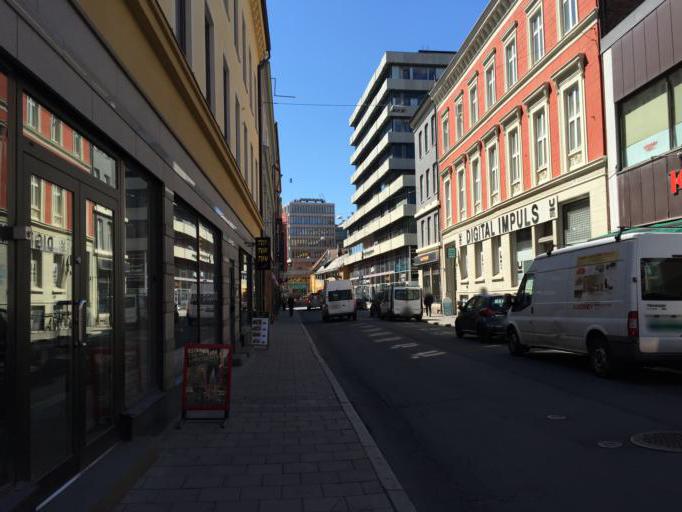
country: NO
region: Oslo
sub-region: Oslo
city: Oslo
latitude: 59.9142
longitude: 10.7466
